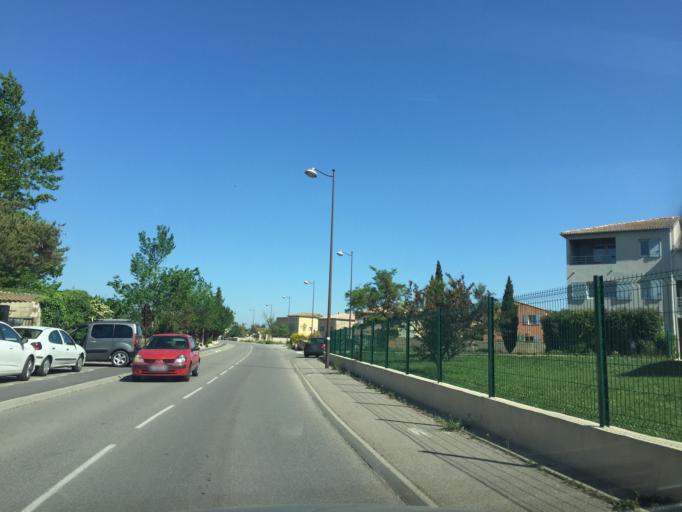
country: FR
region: Provence-Alpes-Cote d'Azur
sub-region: Departement du Vaucluse
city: L'Isle-sur-la-Sorgue
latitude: 43.9230
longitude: 5.0397
